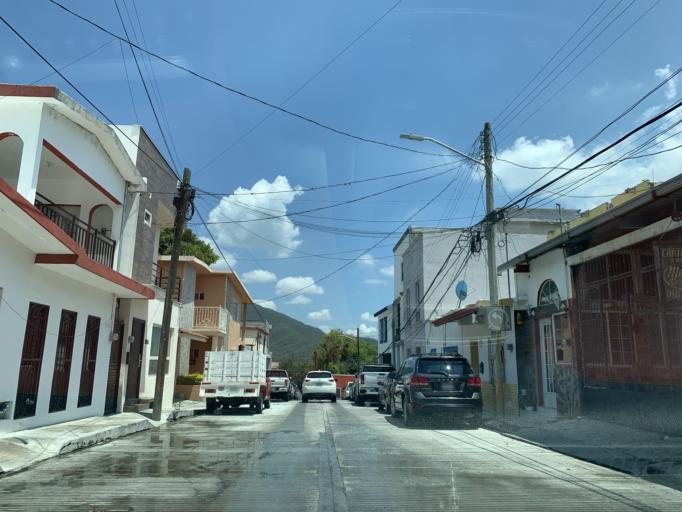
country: MX
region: Nuevo Leon
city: Santiago
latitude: 25.4221
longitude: -100.1494
